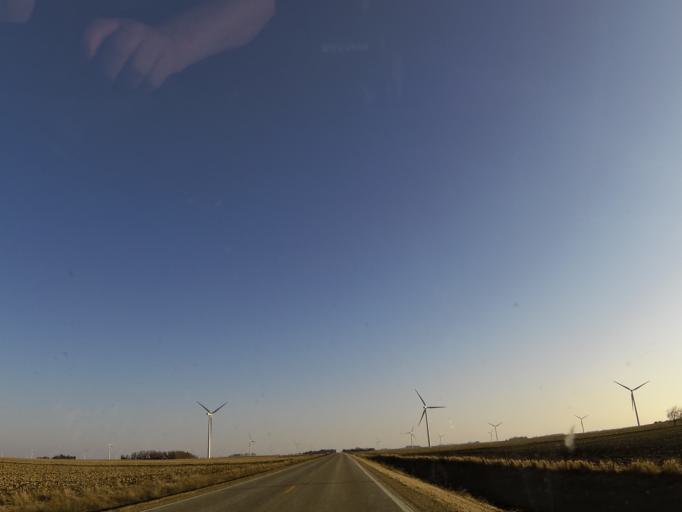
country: US
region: Iowa
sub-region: Worth County
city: Northwood
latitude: 43.4311
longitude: -93.1244
